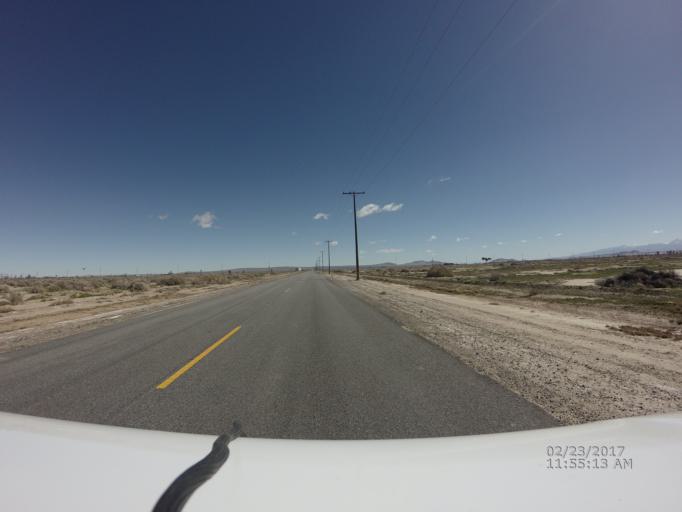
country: US
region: California
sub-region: Los Angeles County
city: Lancaster
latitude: 34.7342
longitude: -117.9759
